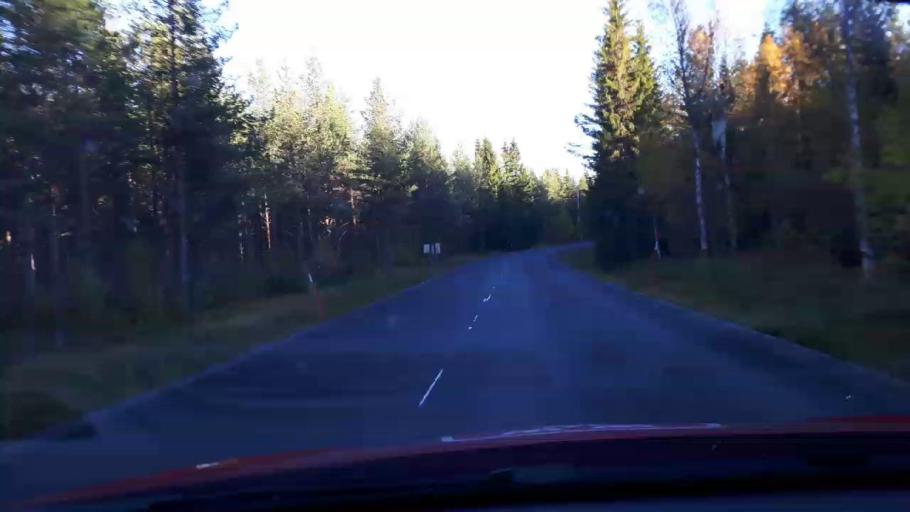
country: SE
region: Jaemtland
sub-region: OEstersunds Kommun
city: Lit
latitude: 63.4149
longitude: 14.8746
